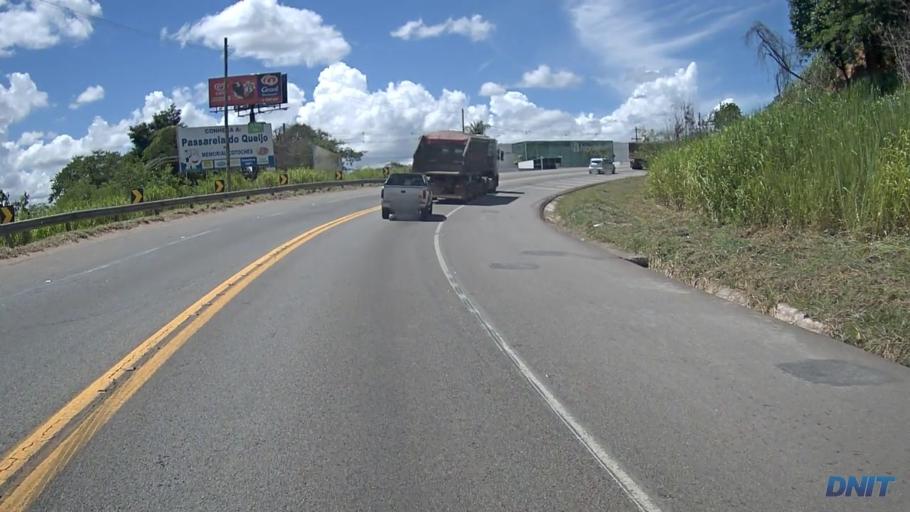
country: BR
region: Minas Gerais
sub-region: Santa Luzia
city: Santa Luzia
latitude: -19.8360
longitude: -43.8615
